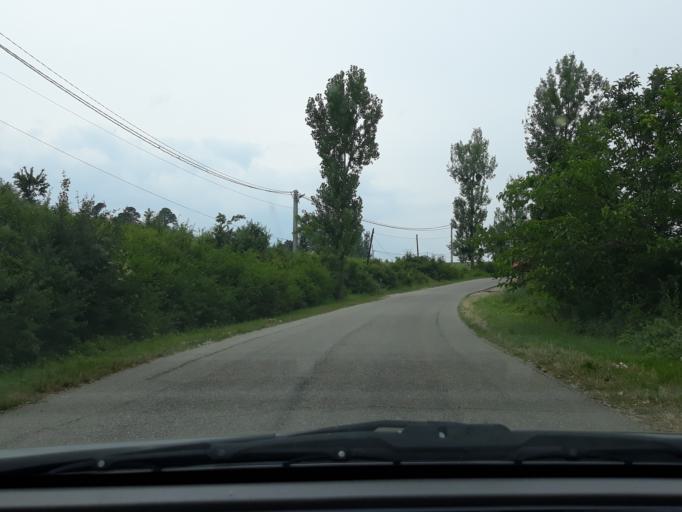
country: RO
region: Salaj
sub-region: Comuna Criseni
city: Criseni
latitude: 47.2470
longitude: 23.0700
